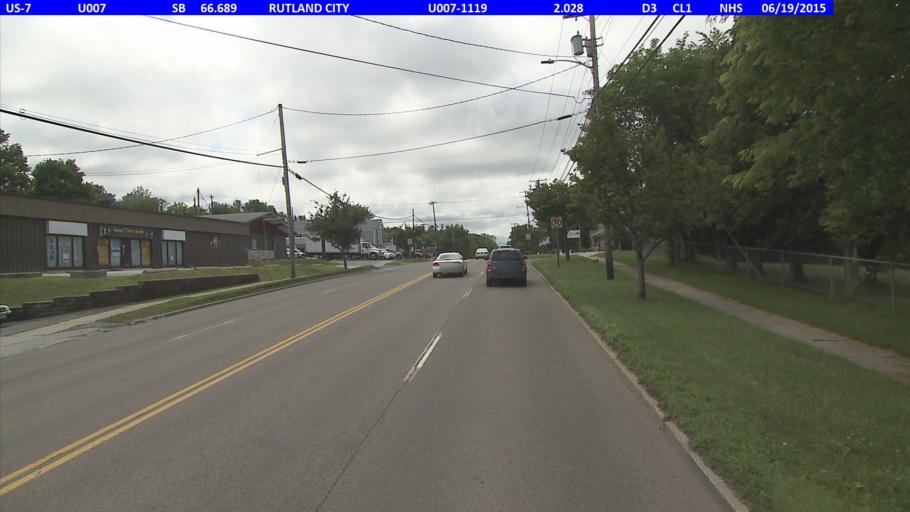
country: US
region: Vermont
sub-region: Rutland County
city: Rutland
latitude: 43.6194
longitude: -72.9743
